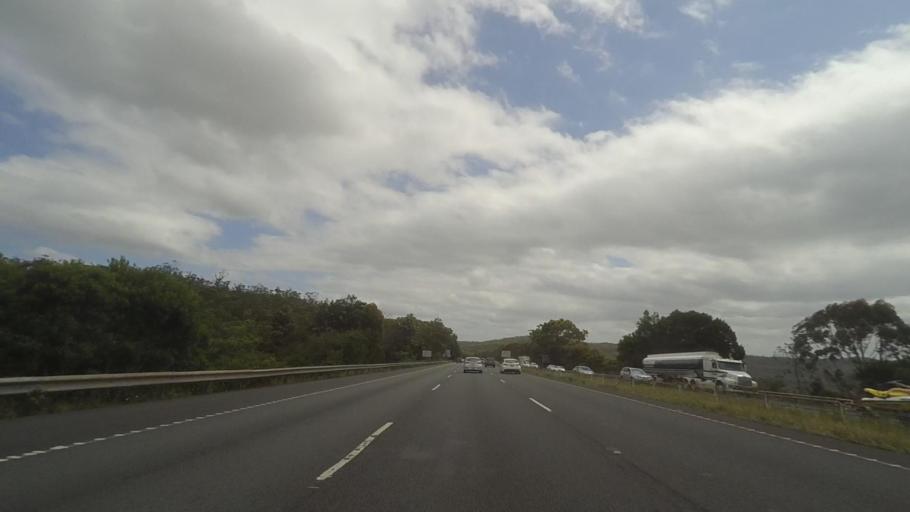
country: AU
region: New South Wales
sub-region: Gosford Shire
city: Point Clare
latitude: -33.4344
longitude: 151.2219
